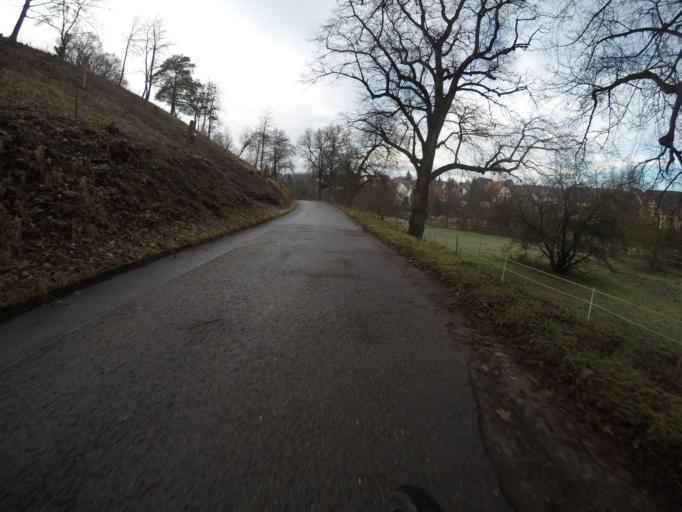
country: DE
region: Baden-Wuerttemberg
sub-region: Regierungsbezirk Stuttgart
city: Ehningen
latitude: 48.6966
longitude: 8.9435
